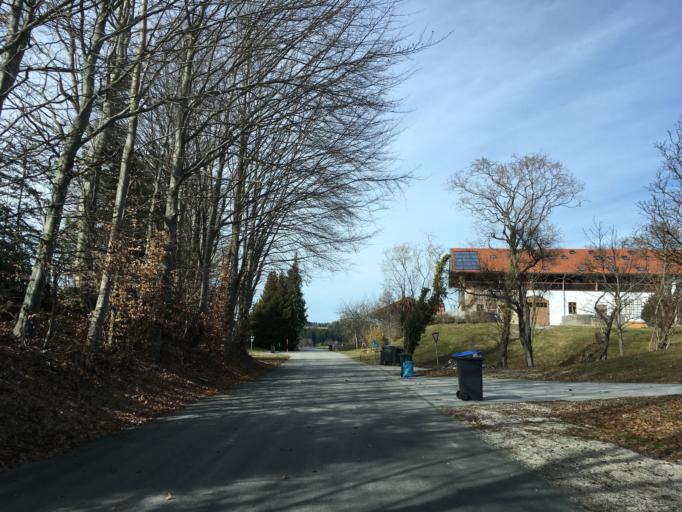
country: DE
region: Bavaria
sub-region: Upper Bavaria
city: Aschau im Chiemgau
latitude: 47.8013
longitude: 12.3405
